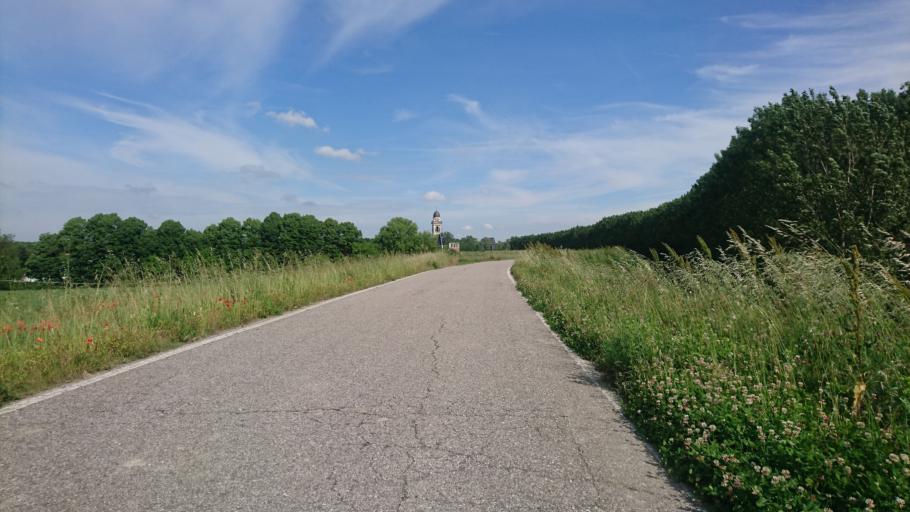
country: IT
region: Lombardy
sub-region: Provincia di Mantova
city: Borgofranco sul Po
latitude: 45.0490
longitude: 11.2096
